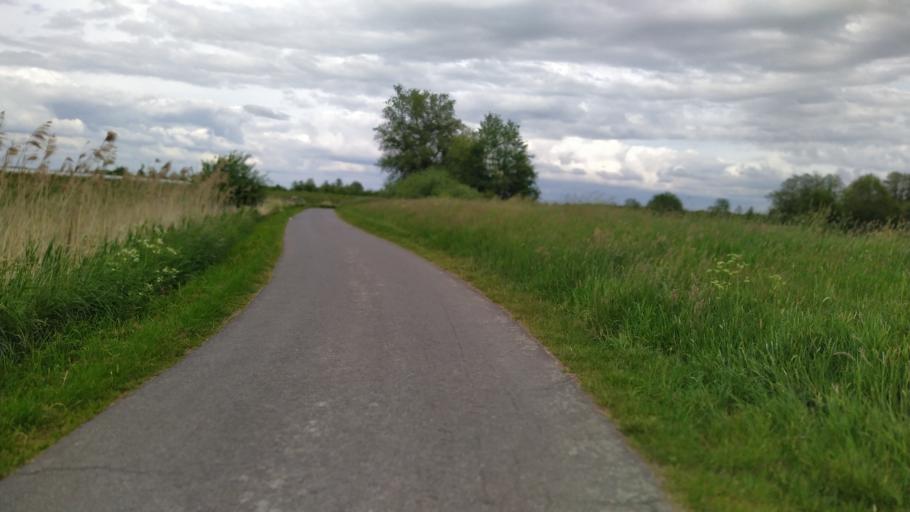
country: DE
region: Lower Saxony
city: Buxtehude
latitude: 53.4913
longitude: 9.7351
